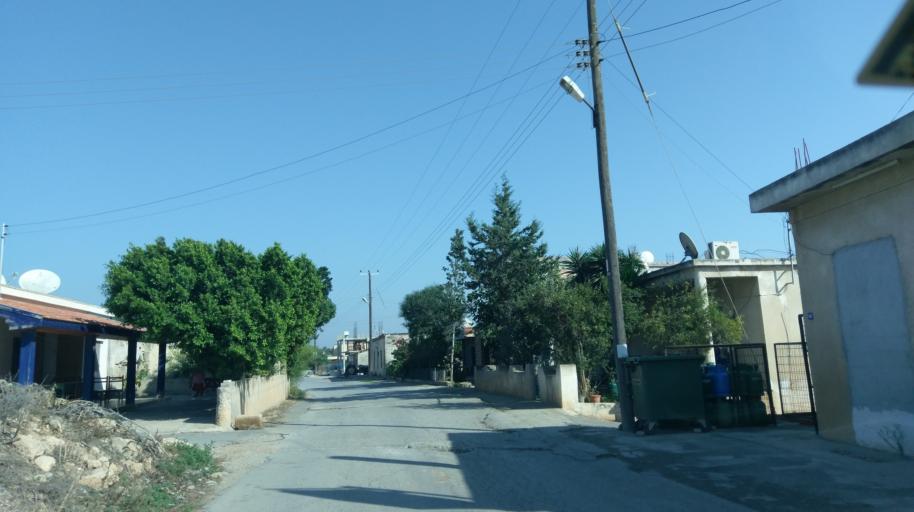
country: CY
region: Ammochostos
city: Leonarisso
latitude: 35.4726
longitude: 34.1520
